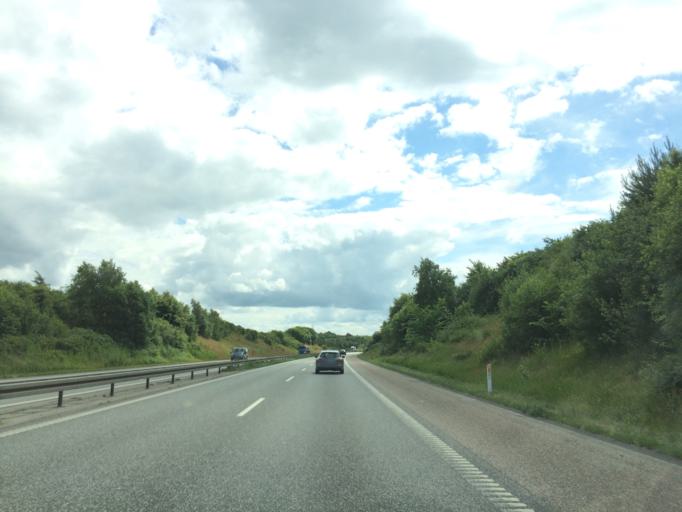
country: DK
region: North Denmark
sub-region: Mariagerfjord Kommune
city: Hobro
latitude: 56.7094
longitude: 9.7285
